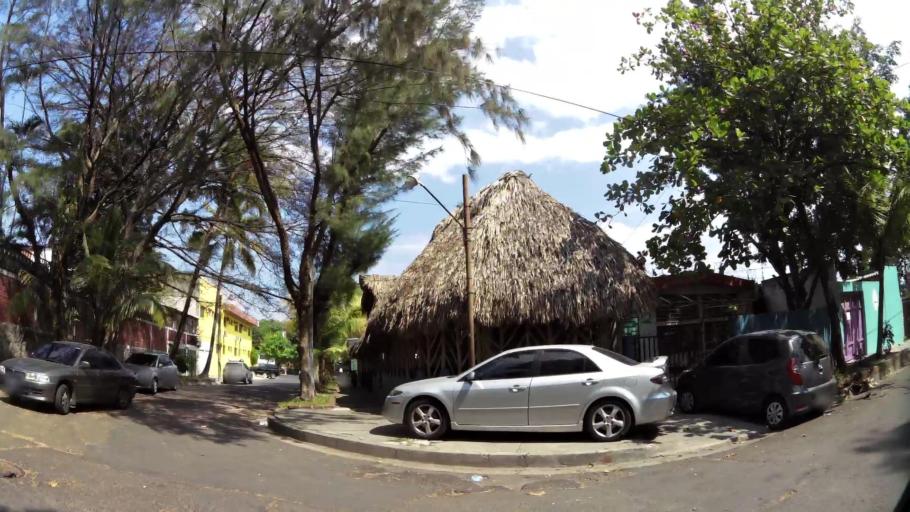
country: SV
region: San Salvador
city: Mejicanos
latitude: 13.7091
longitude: -89.2144
